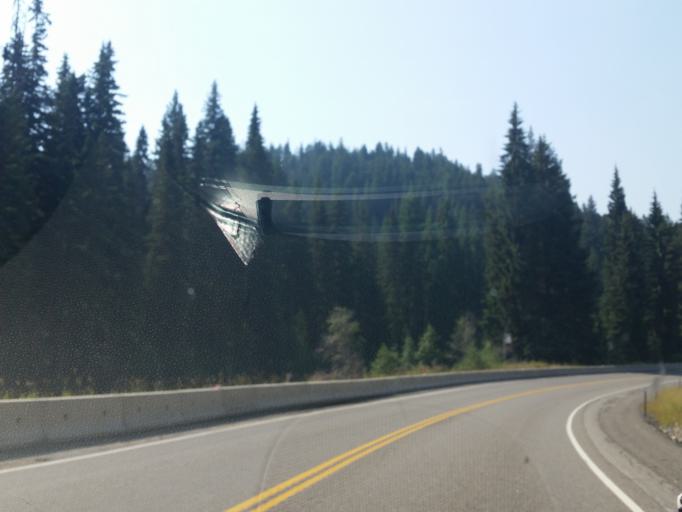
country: CA
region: British Columbia
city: Princeton
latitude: 49.1545
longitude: -120.5872
